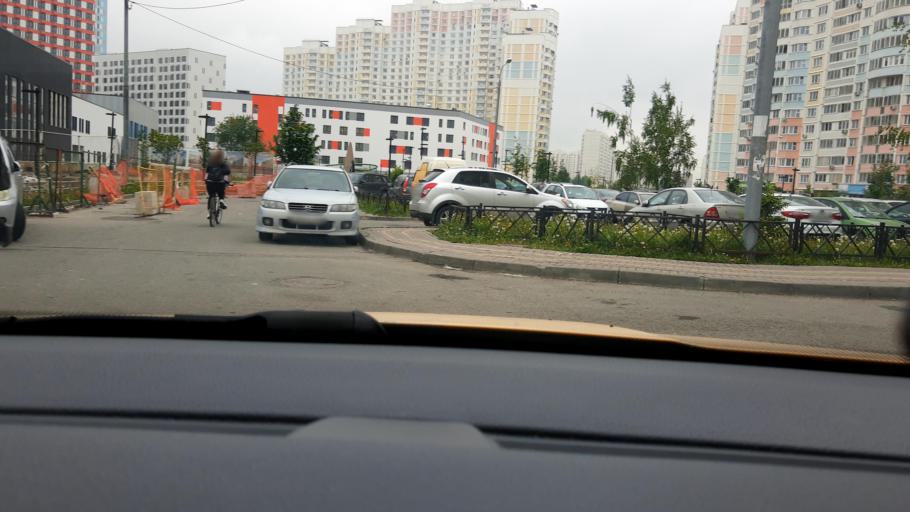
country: RU
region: Moskovskaya
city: Mytishchi
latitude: 55.9159
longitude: 37.7142
